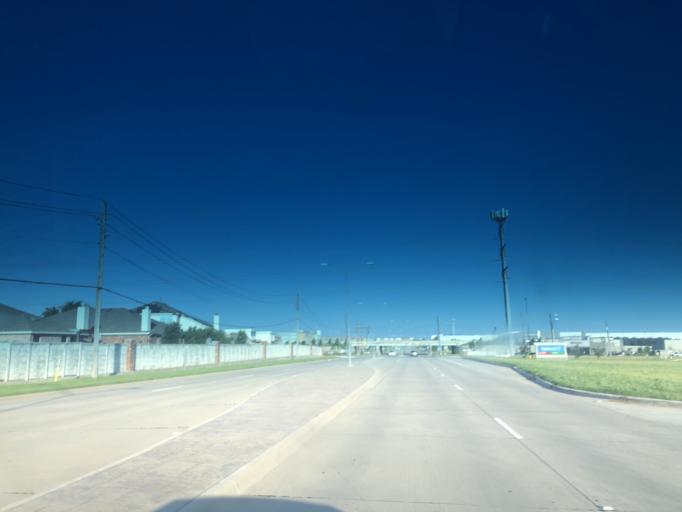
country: US
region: Texas
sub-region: Dallas County
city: Grand Prairie
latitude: 32.7055
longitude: -97.0208
